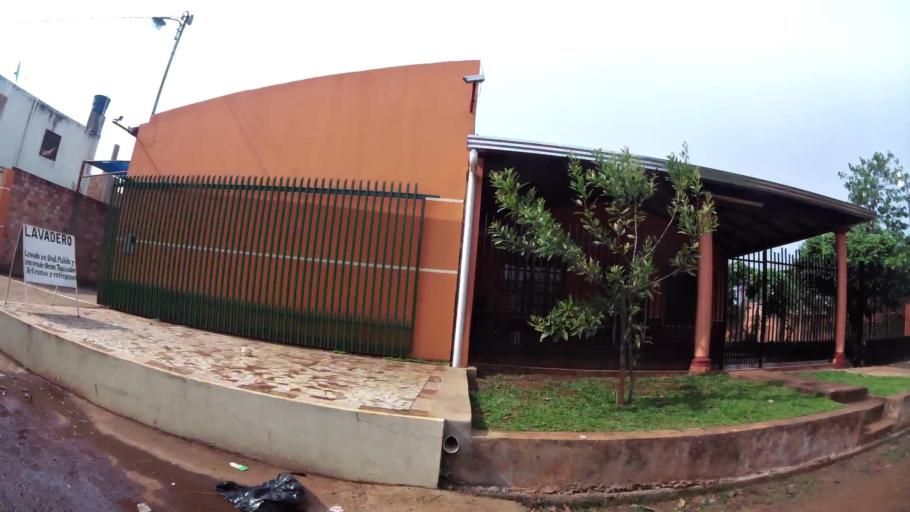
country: PY
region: Alto Parana
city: Ciudad del Este
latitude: -25.4892
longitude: -54.6464
